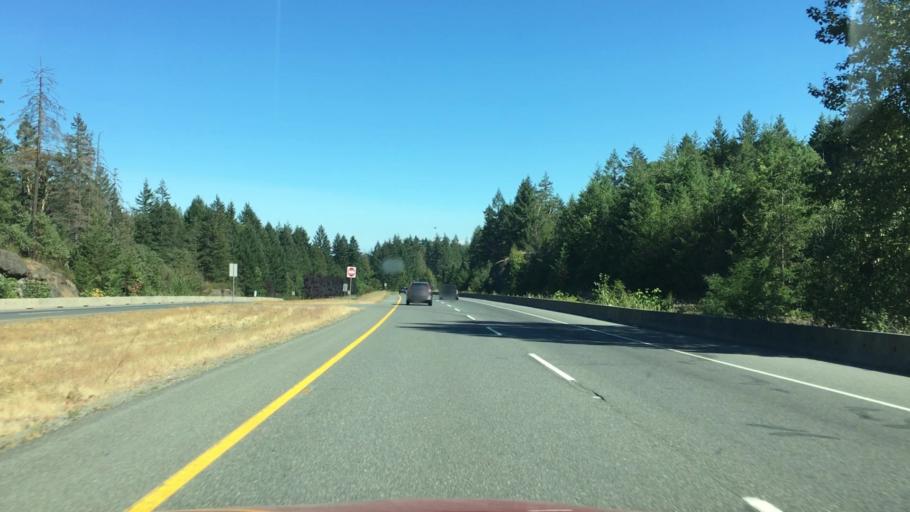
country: CA
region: British Columbia
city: Nanaimo
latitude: 49.1409
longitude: -123.9627
